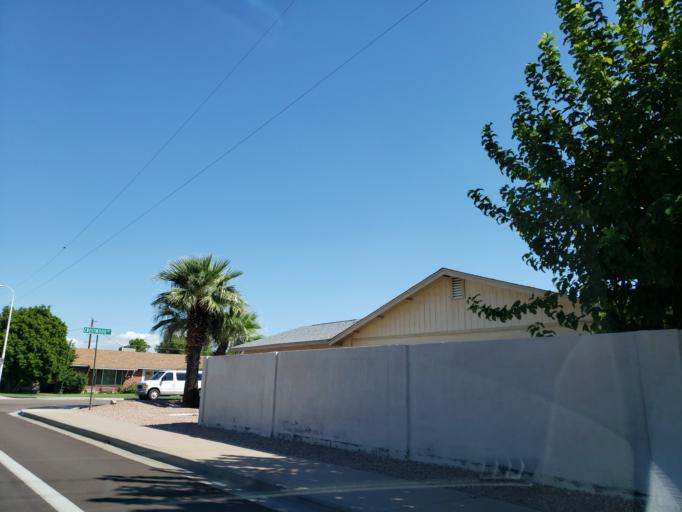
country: US
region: Arizona
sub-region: Maricopa County
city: Scottsdale
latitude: 33.5135
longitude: -111.9002
